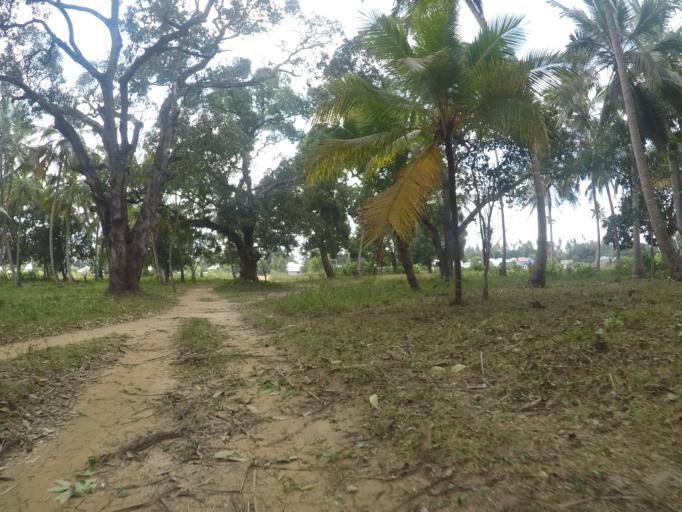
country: TZ
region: Zanzibar Urban/West
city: Zanzibar
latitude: -6.2055
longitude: 39.2389
